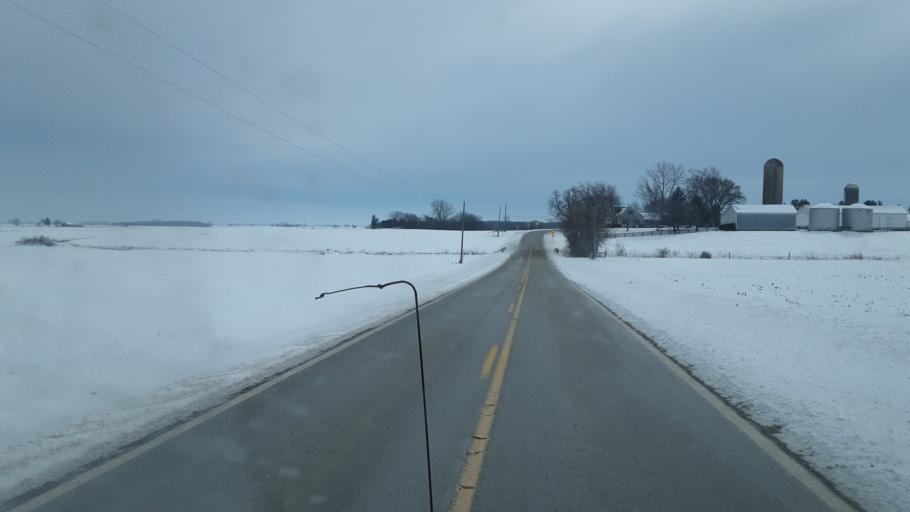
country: US
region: Ohio
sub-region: Madison County
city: Choctaw Lake
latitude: 40.0062
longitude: -83.5008
